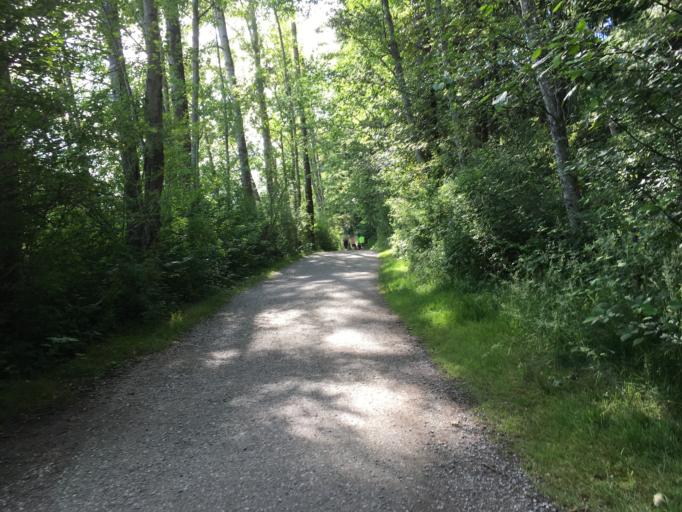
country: US
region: Washington
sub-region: Whatcom County
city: Geneva
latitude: 48.7059
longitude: -122.4495
